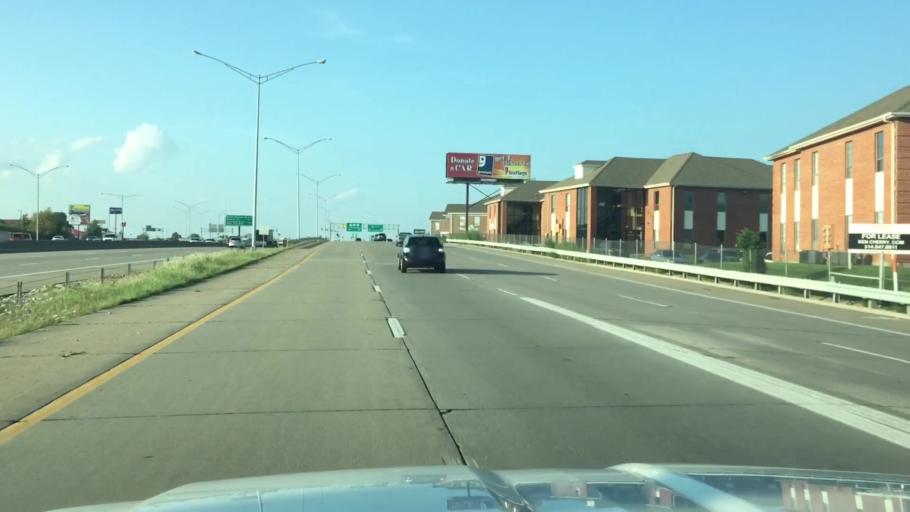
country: US
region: Missouri
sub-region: Saint Louis County
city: Mehlville
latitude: 38.5066
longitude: -90.3370
